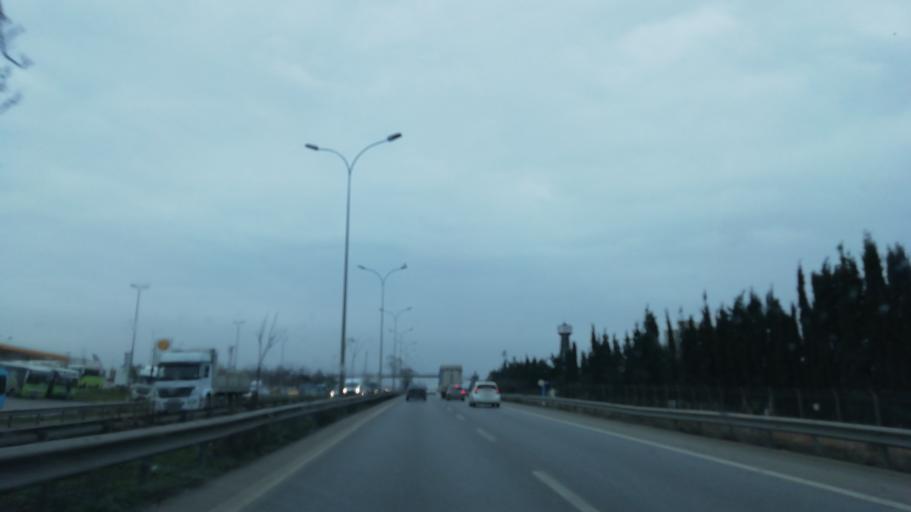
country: TR
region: Istanbul
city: Icmeler
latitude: 40.8241
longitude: 29.3507
